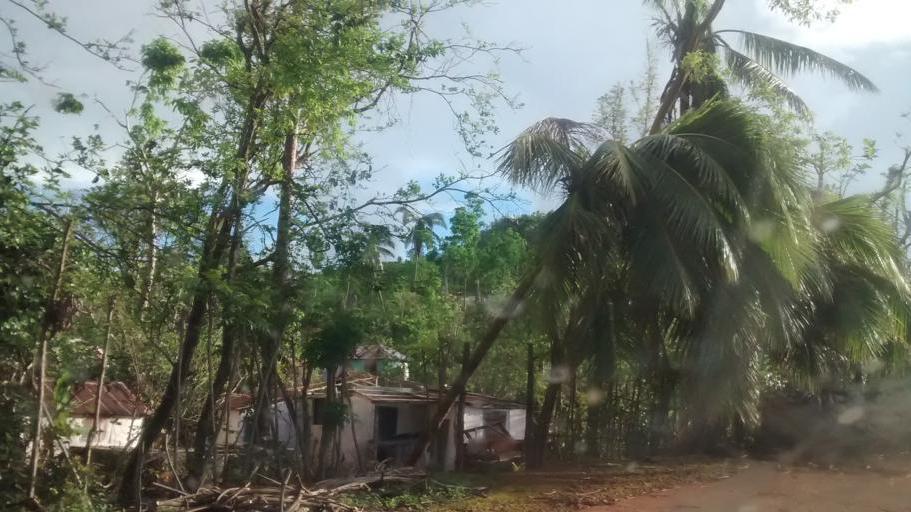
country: HT
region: Grandans
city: Corail
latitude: 18.5149
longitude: -73.7846
